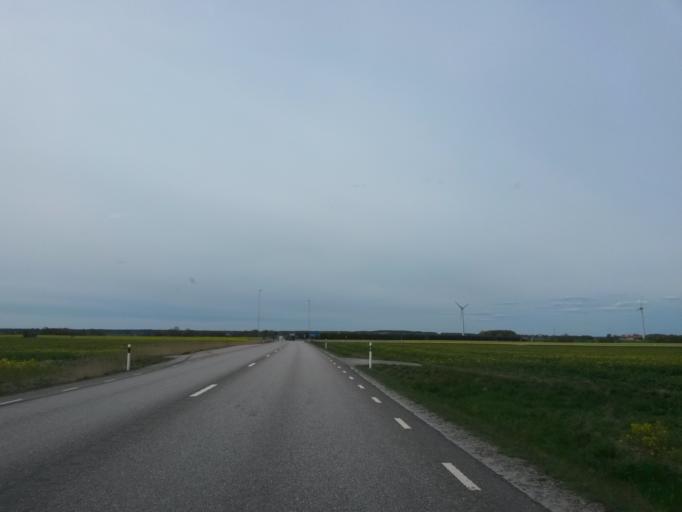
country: SE
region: Vaestra Goetaland
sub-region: Vara Kommun
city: Vara
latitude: 58.2957
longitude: 12.9558
